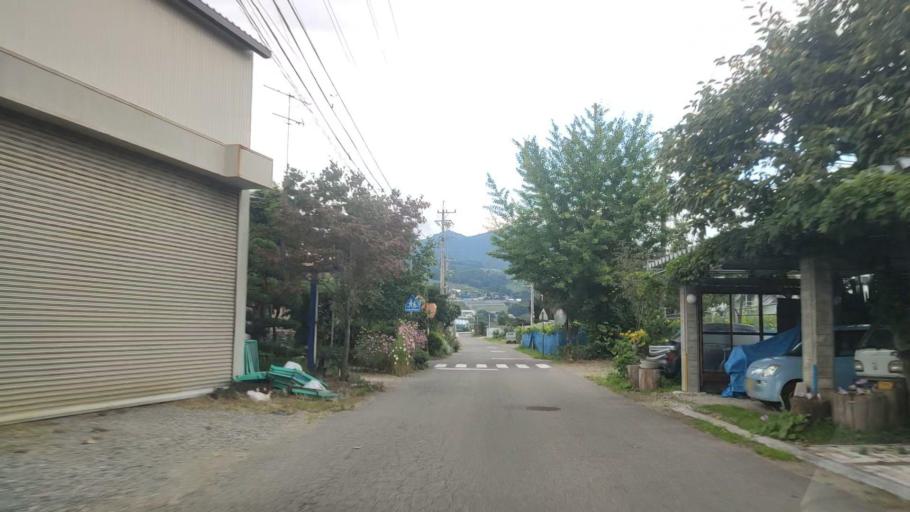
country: JP
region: Nagano
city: Nakano
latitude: 36.7624
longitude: 138.3926
